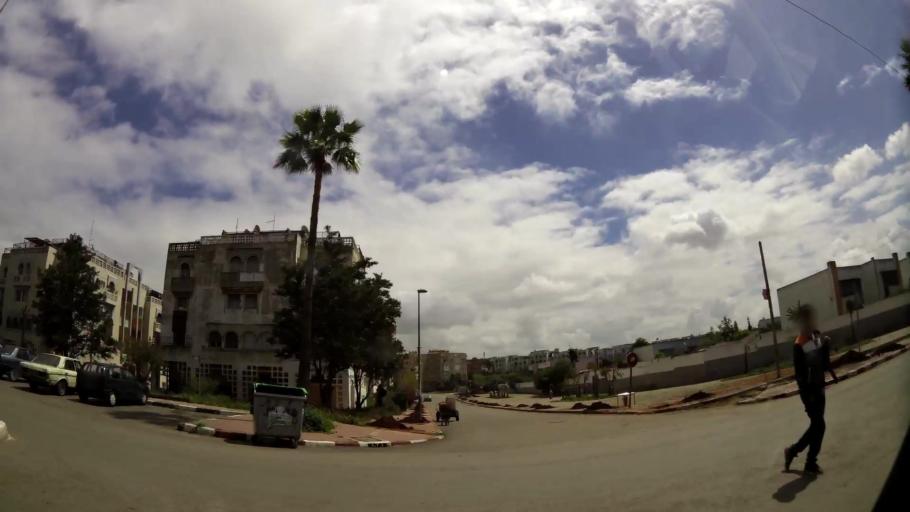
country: MA
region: Grand Casablanca
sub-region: Mediouna
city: Tit Mellil
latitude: 33.6055
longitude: -7.5219
